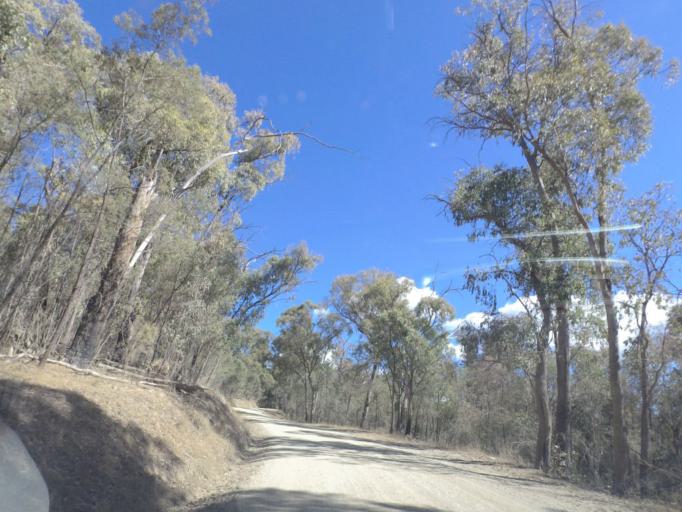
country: AU
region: Victoria
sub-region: Murrindindi
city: Alexandra
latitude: -37.3226
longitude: 145.8079
